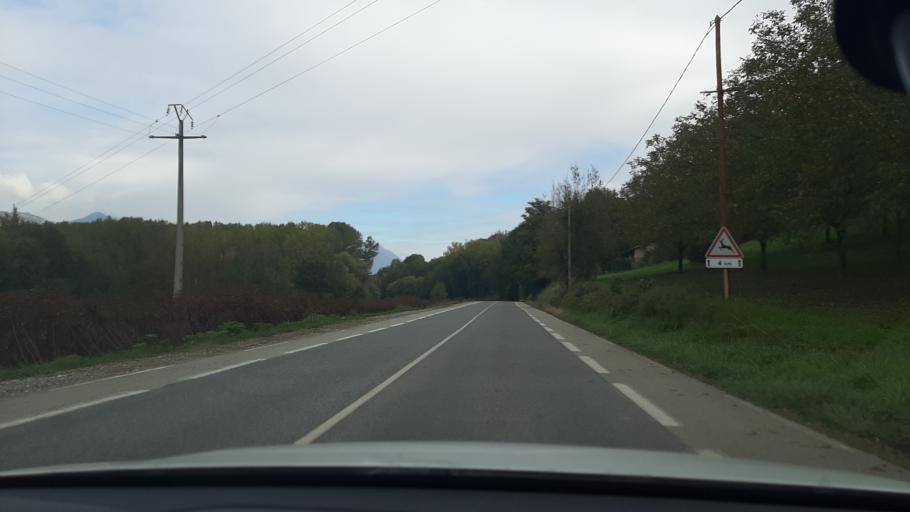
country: FR
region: Rhone-Alpes
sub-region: Departement de l'Isere
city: Pontcharra
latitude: 45.4523
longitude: 6.0435
